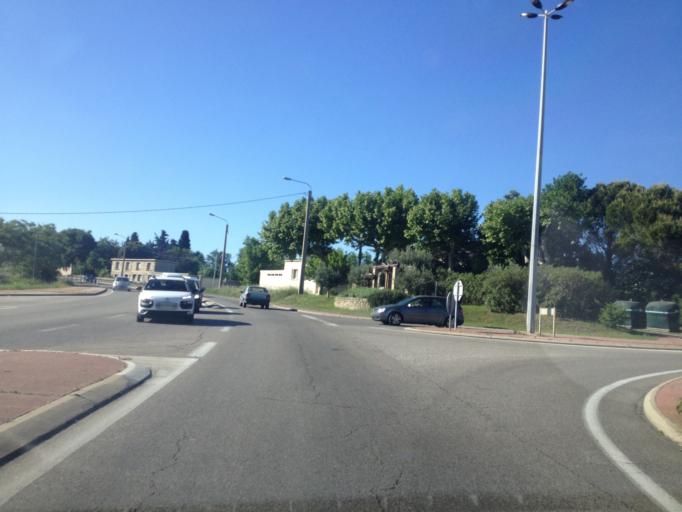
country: FR
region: Provence-Alpes-Cote d'Azur
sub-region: Departement du Vaucluse
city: Courthezon
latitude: 44.0913
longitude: 4.8779
